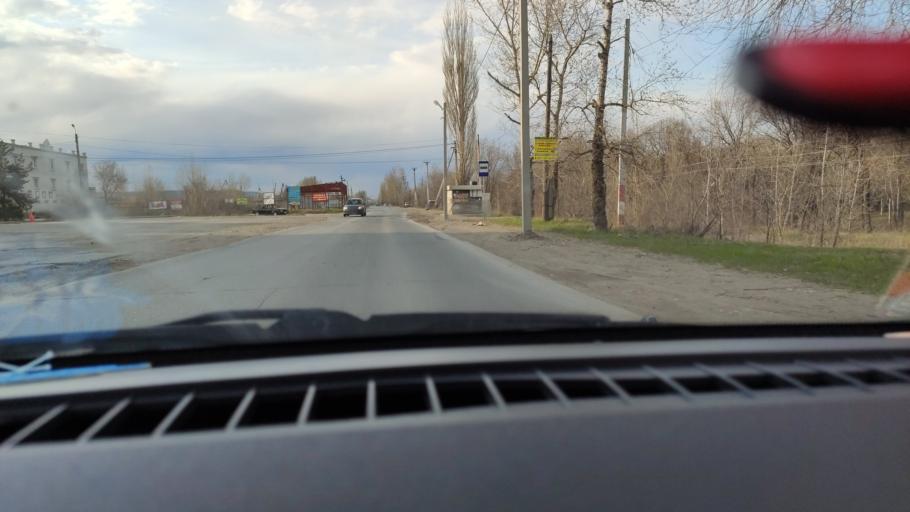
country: RU
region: Saratov
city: Engel's
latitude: 51.4820
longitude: 46.0560
